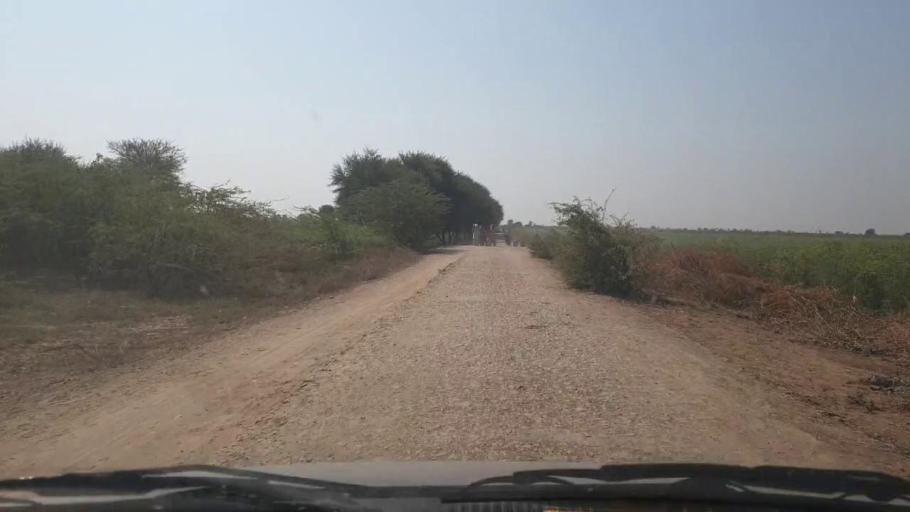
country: PK
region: Sindh
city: Samaro
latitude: 25.2685
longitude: 69.3221
